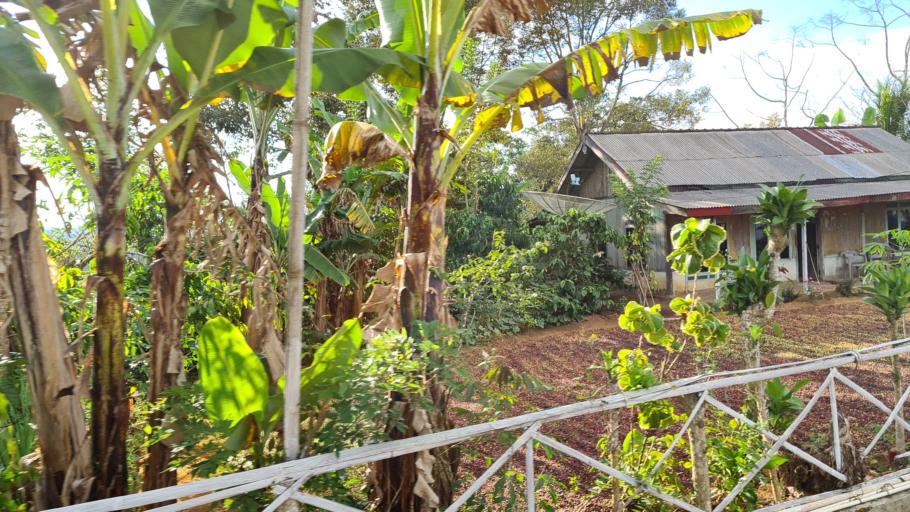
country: ID
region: Lampung
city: Kenali
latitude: -5.0939
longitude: 104.3990
